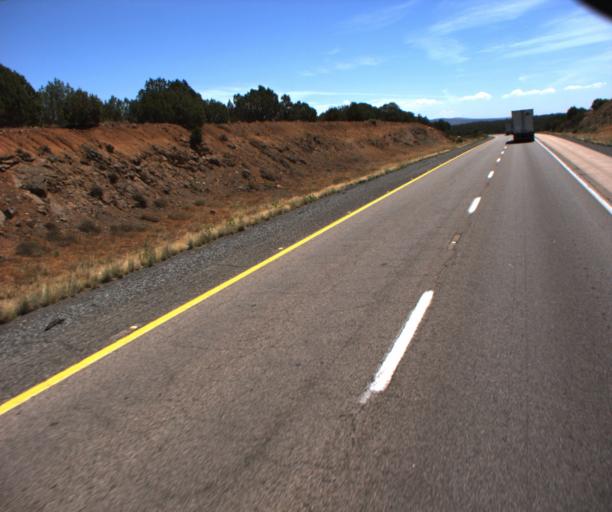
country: US
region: Arizona
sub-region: Mohave County
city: Peach Springs
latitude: 35.2073
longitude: -113.2798
